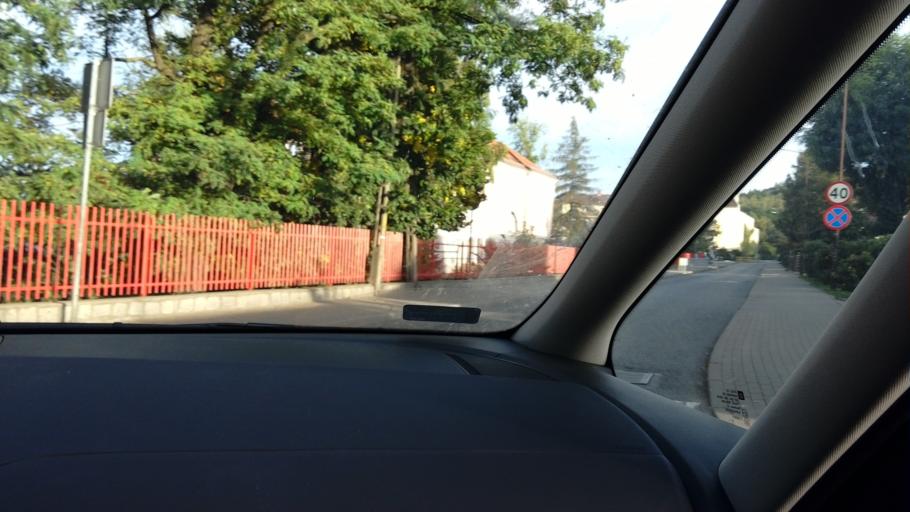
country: PL
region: Lower Silesian Voivodeship
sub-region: Jelenia Gora
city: Jelenia Gora
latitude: 50.8898
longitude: 15.7318
